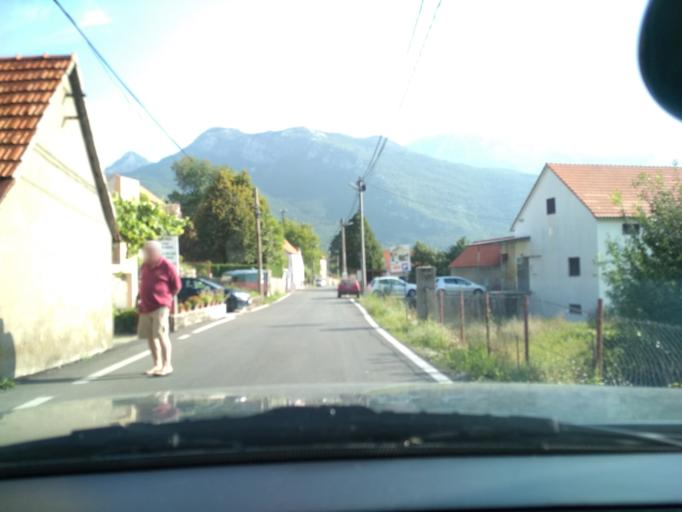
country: ME
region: Kotor
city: Kotor
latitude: 42.4349
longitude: 18.8296
